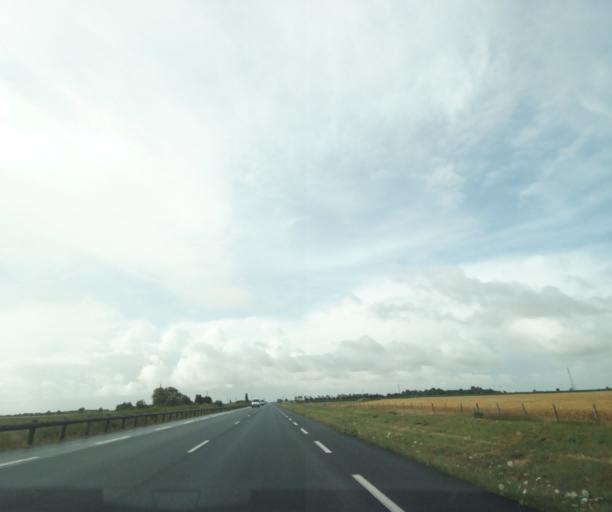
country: FR
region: Pays de la Loire
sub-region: Departement de la Vendee
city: Champagne-les-Marais
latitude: 46.3600
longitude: -1.0873
